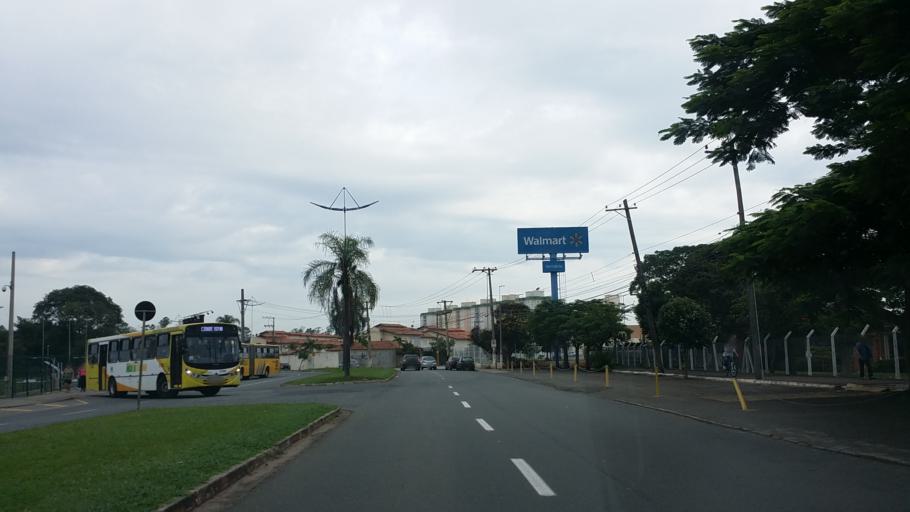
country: BR
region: Sao Paulo
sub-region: Indaiatuba
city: Indaiatuba
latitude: -23.1152
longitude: -47.2182
